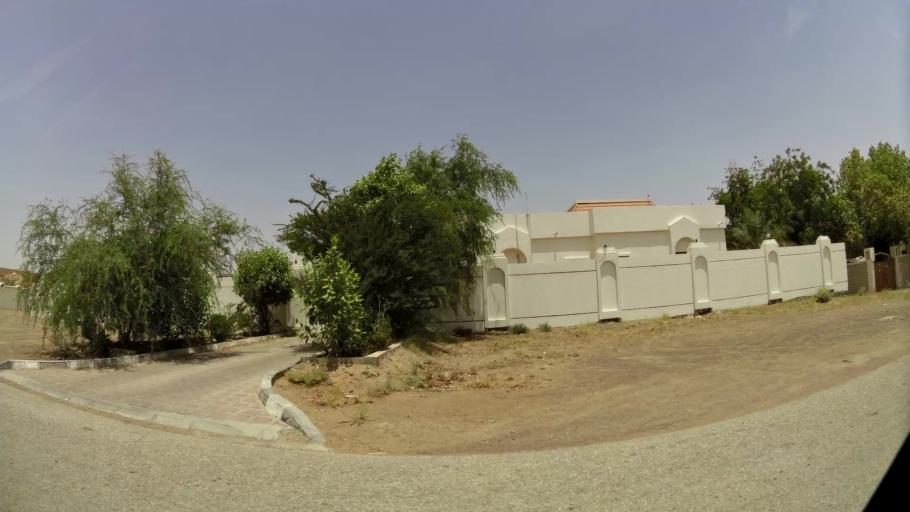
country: AE
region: Abu Dhabi
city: Al Ain
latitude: 24.2089
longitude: 55.7330
